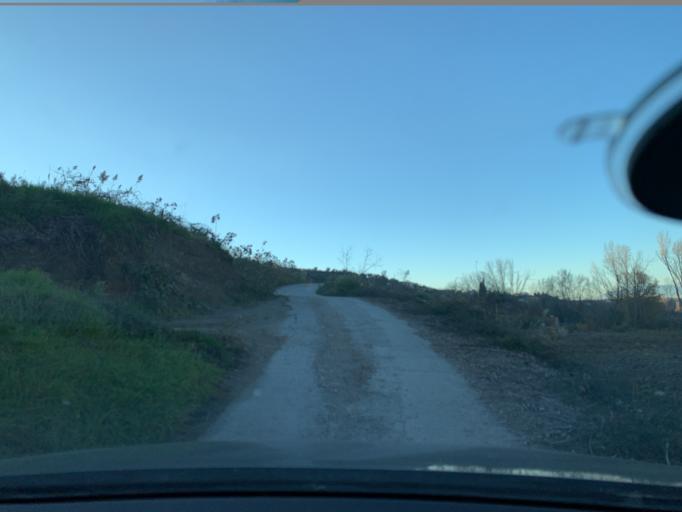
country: ES
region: Andalusia
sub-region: Provincia de Granada
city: Dilar
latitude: 37.0736
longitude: -3.5923
